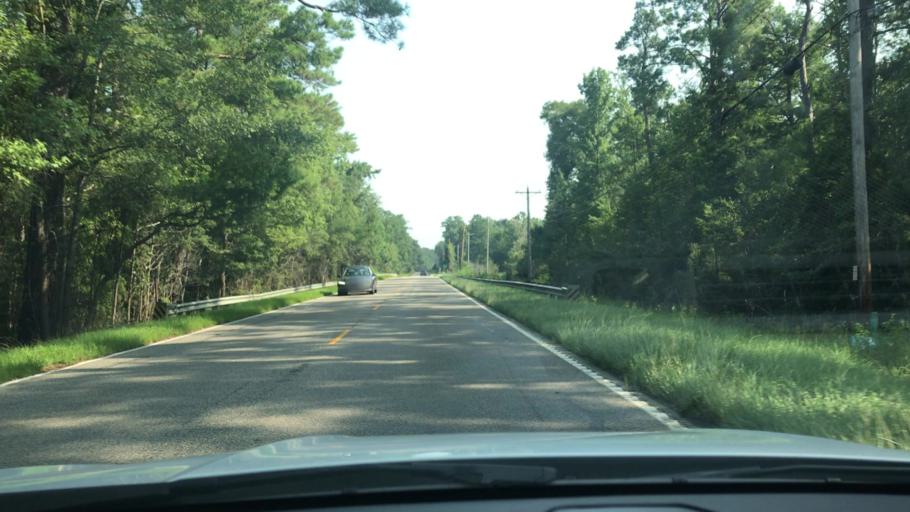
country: US
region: South Carolina
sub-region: Georgetown County
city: Georgetown
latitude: 33.4677
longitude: -79.2798
